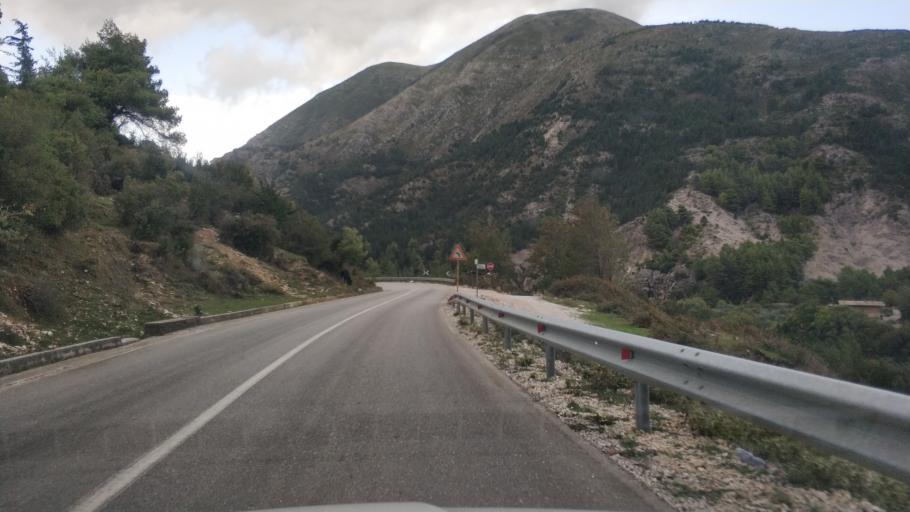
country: AL
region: Vlore
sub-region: Rrethi i Vlores
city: Orikum
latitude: 40.2435
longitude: 19.5509
